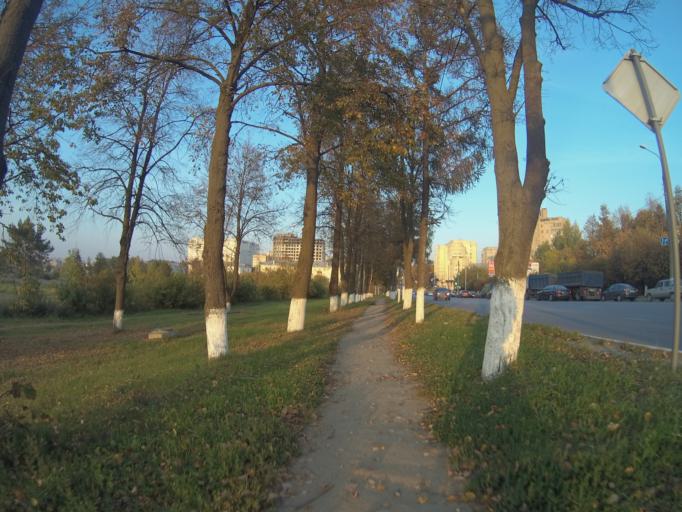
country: RU
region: Vladimir
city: Vladimir
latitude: 56.1155
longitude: 40.3403
